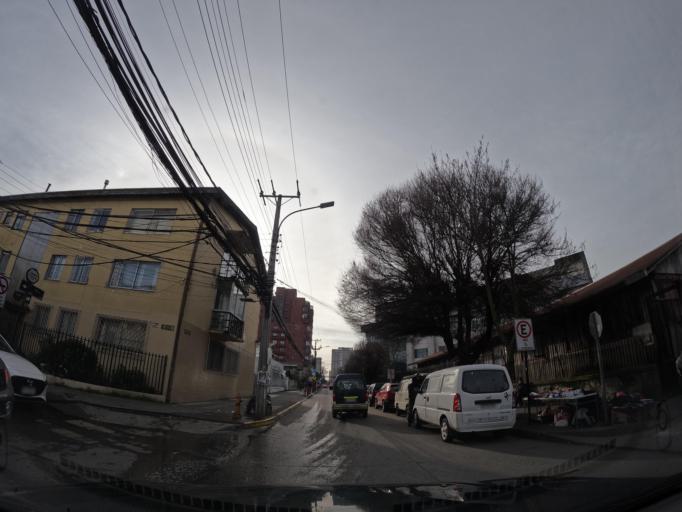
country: CL
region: Biobio
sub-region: Provincia de Concepcion
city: Concepcion
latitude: -36.8257
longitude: -73.0392
